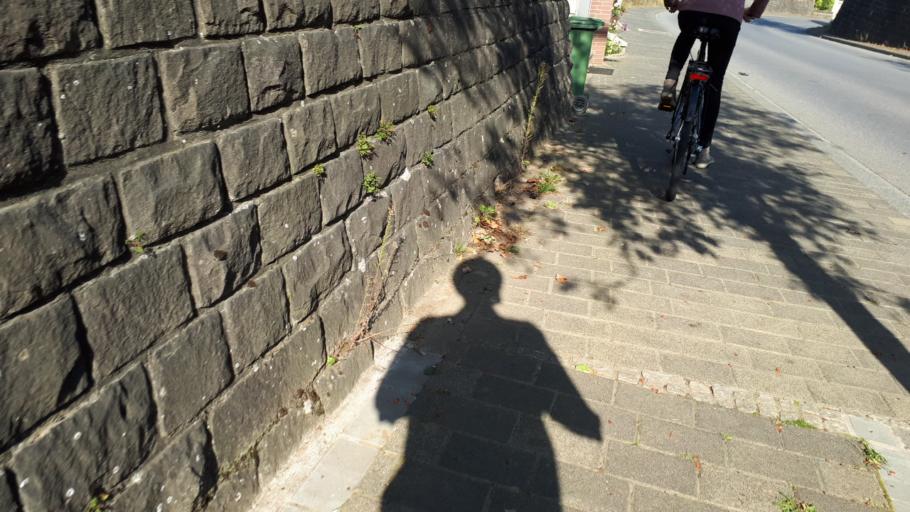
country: LU
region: Luxembourg
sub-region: Canton de Capellen
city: Mamer
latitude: 49.6277
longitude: 6.0192
